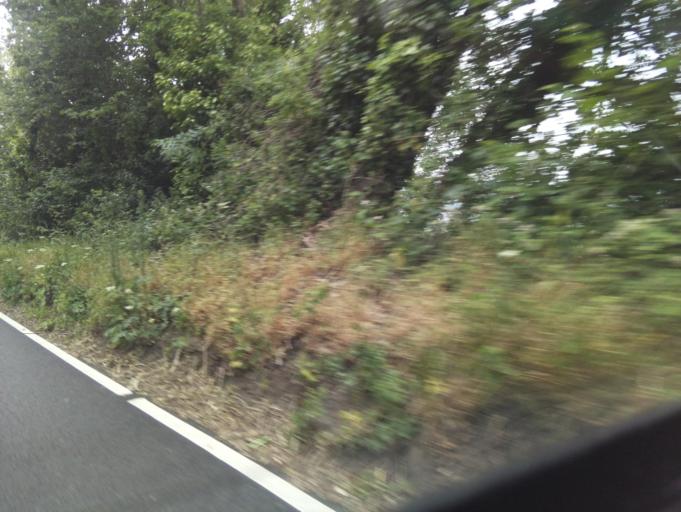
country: GB
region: England
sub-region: Devon
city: Colyton
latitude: 50.7260
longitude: -3.0305
